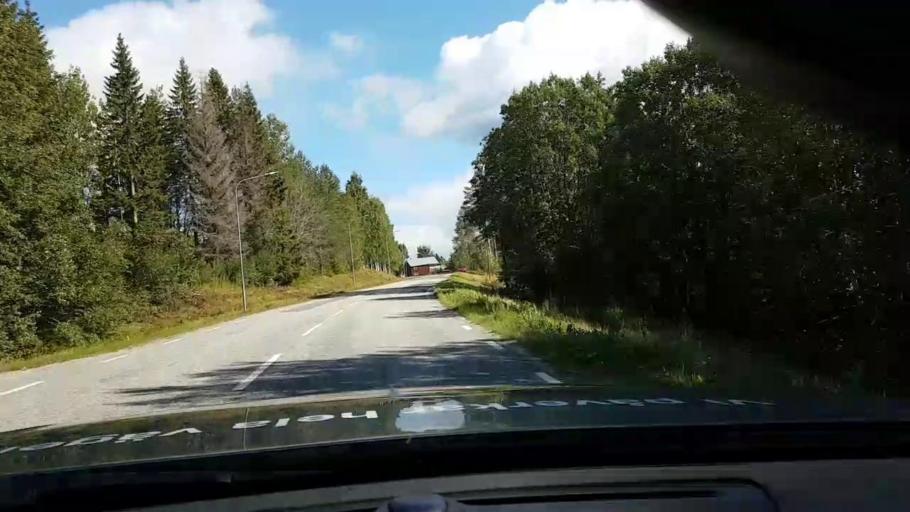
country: SE
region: Vaesterbotten
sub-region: Asele Kommun
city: Asele
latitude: 63.7918
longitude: 17.6210
